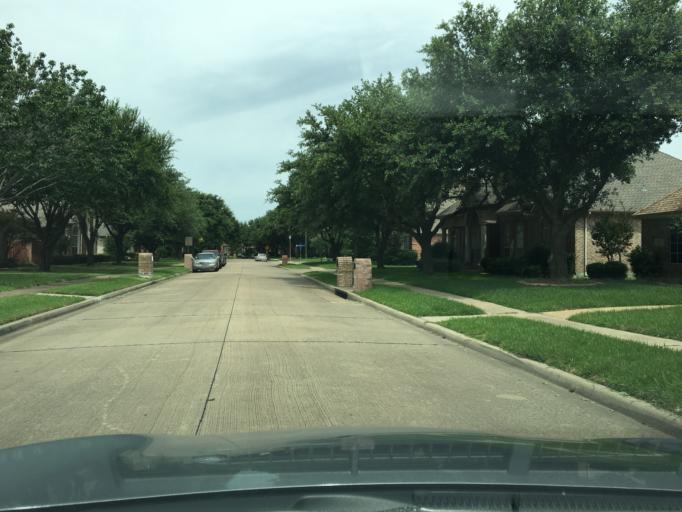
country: US
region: Texas
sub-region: Dallas County
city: Richardson
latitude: 32.9361
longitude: -96.7161
